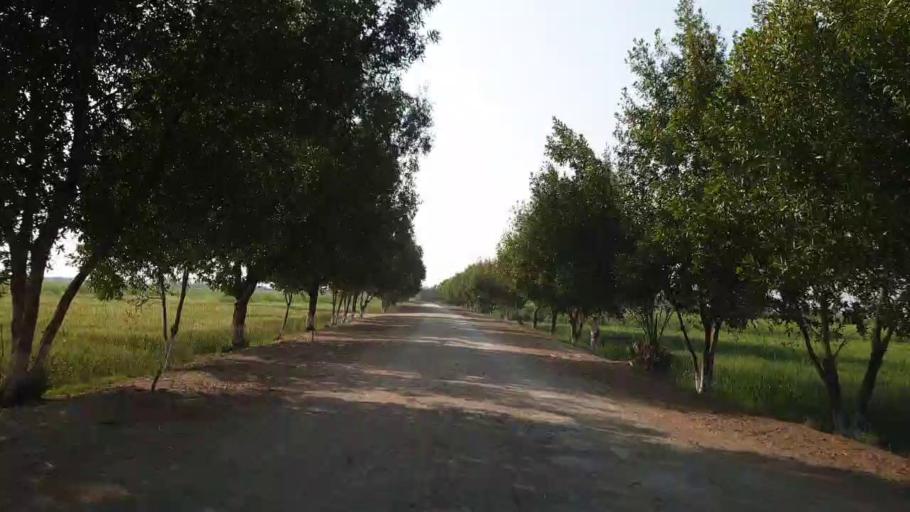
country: PK
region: Sindh
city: Pithoro
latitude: 25.6874
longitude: 69.2060
